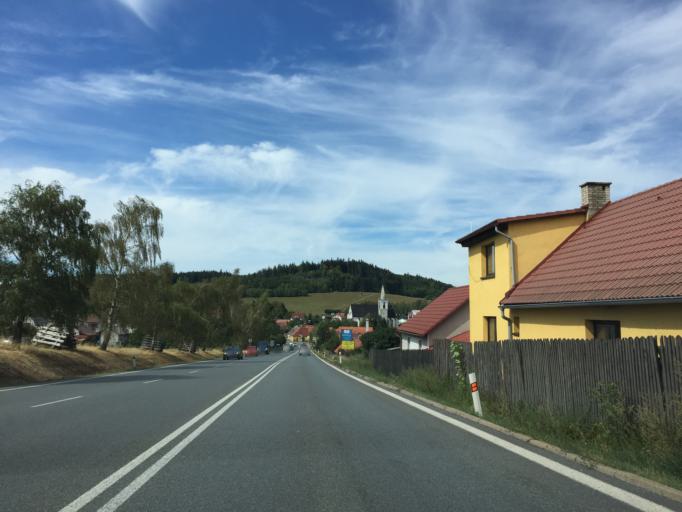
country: CZ
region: Central Bohemia
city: Votice
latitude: 49.5674
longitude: 14.6602
